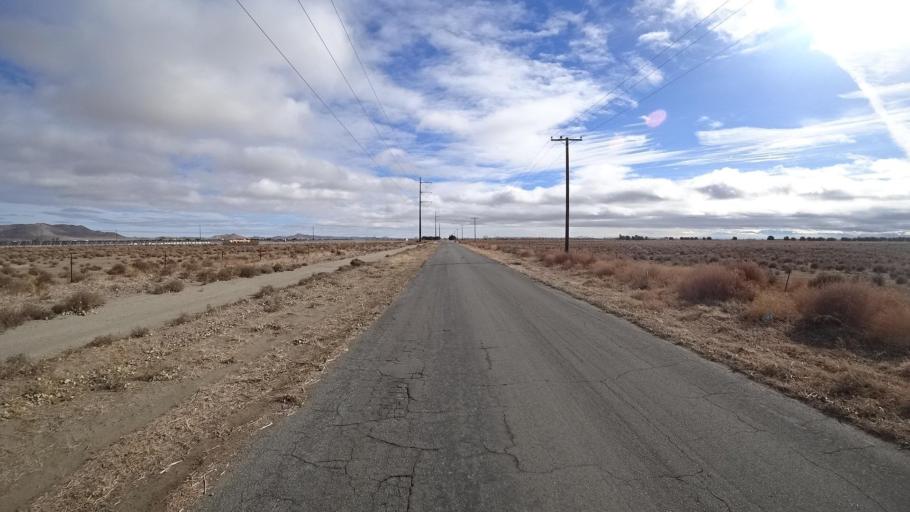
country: US
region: California
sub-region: Kern County
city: Rosamond
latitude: 34.8344
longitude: -118.3168
